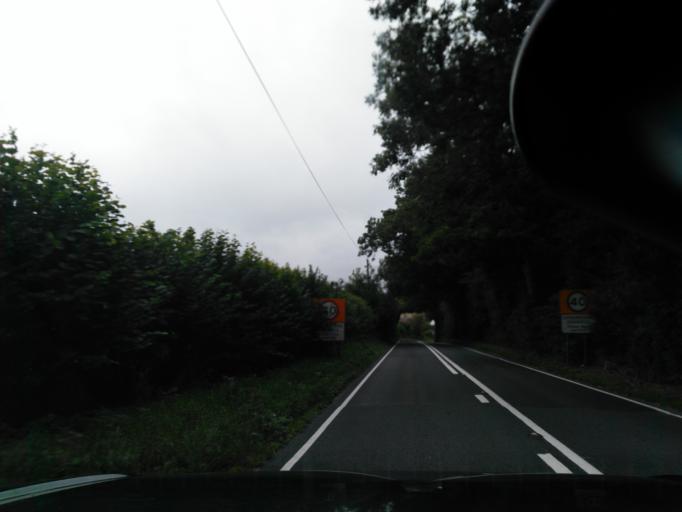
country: GB
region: England
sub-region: Wiltshire
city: Boreham
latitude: 51.1627
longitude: -2.1832
